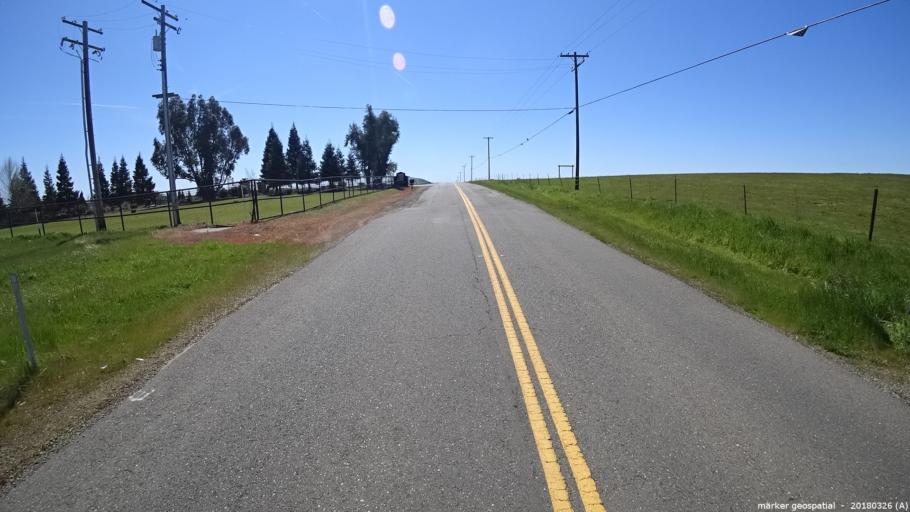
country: US
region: California
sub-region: Sacramento County
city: Wilton
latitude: 38.4850
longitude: -121.2178
